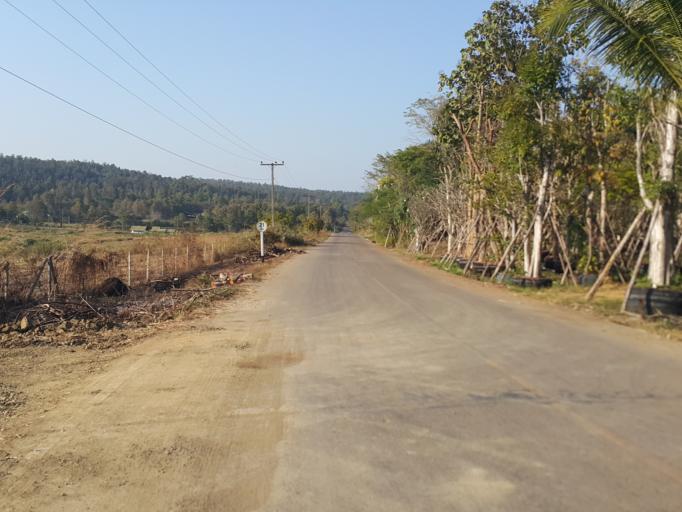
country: TH
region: Chiang Mai
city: Mae On
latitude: 18.8442
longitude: 99.2636
